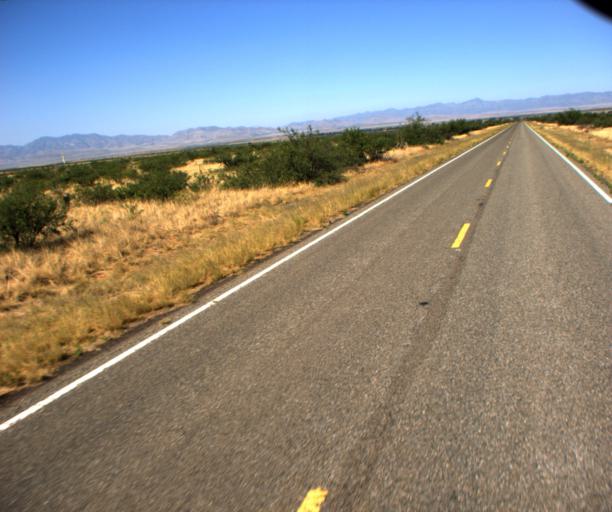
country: US
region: Arizona
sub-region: Graham County
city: Swift Trail Junction
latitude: 32.5844
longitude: -109.9362
